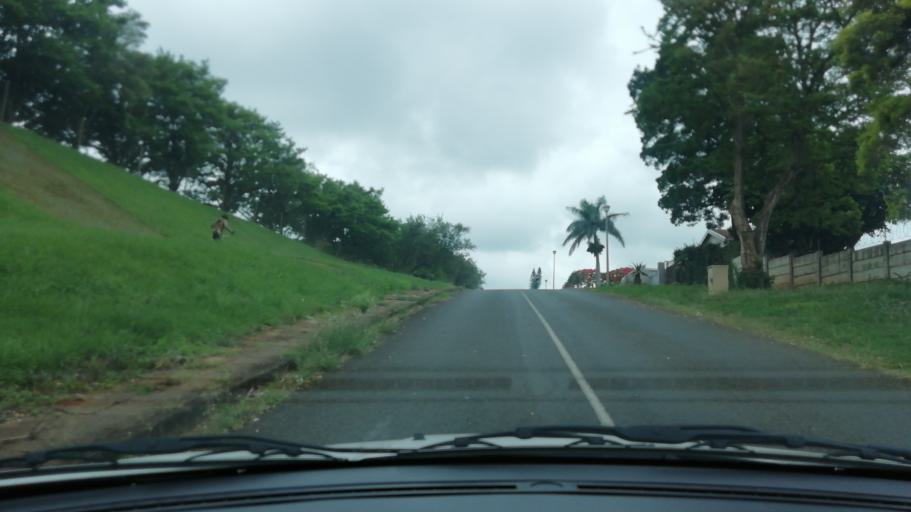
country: ZA
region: KwaZulu-Natal
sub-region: uThungulu District Municipality
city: Empangeni
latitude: -28.7548
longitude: 31.8844
